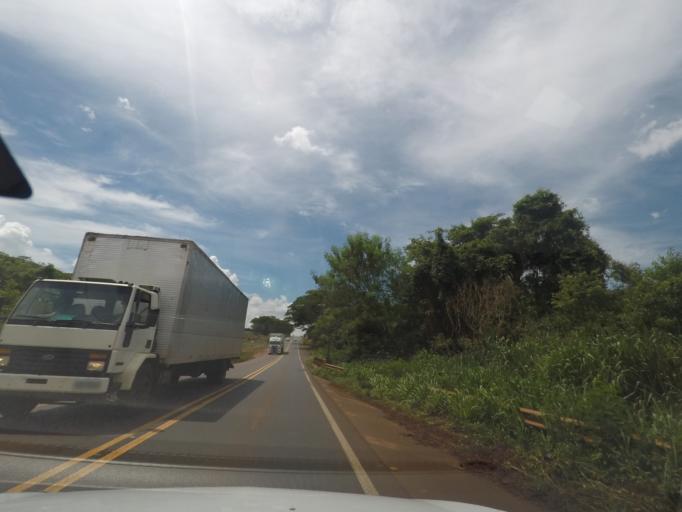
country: BR
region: Sao Paulo
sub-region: Barretos
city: Barretos
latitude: -20.2612
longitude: -48.6748
